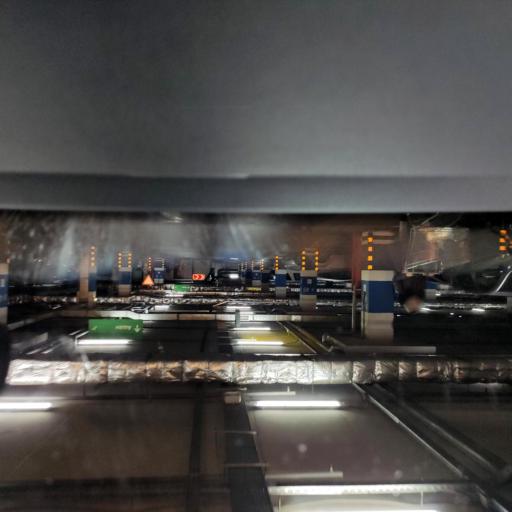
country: RU
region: Moskovskaya
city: Razvilka
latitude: 55.5850
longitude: 37.7224
